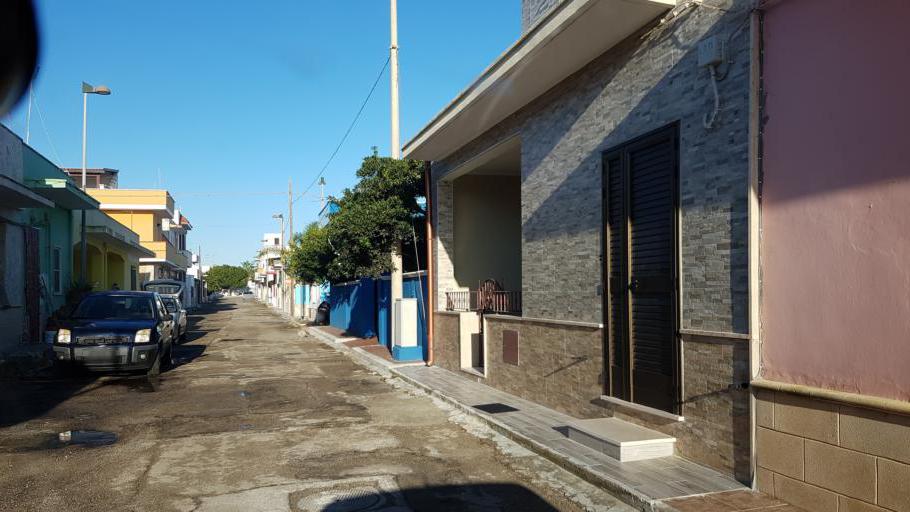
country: IT
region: Apulia
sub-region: Provincia di Brindisi
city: Torchiarolo
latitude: 40.5356
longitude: 18.0736
